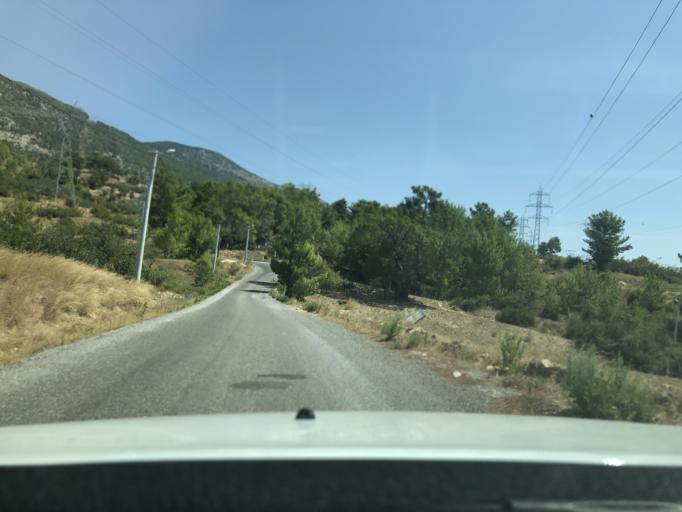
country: TR
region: Antalya
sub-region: Manavgat
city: Manavgat
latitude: 36.8762
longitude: 31.5483
